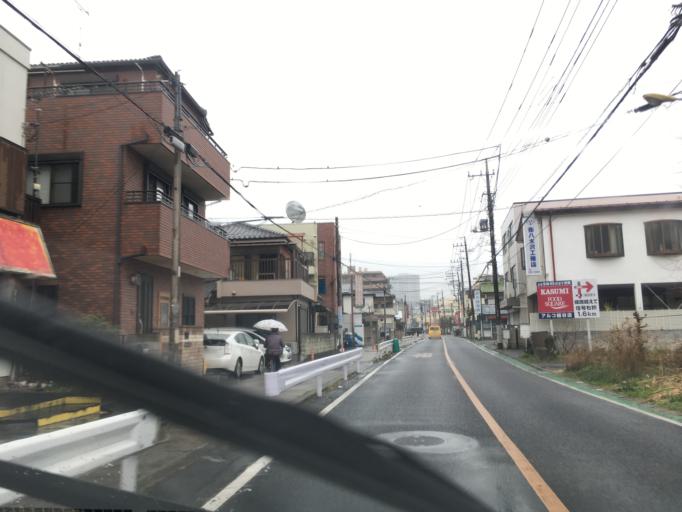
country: JP
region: Saitama
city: Koshigaya
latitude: 35.8804
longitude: 139.7819
